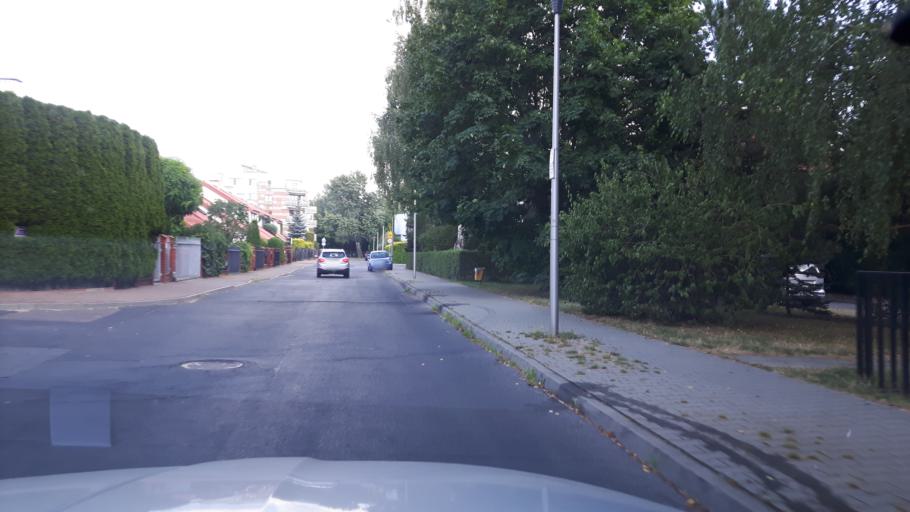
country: PL
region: Masovian Voivodeship
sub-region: Warszawa
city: Praga Poludnie
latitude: 52.2232
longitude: 21.0765
